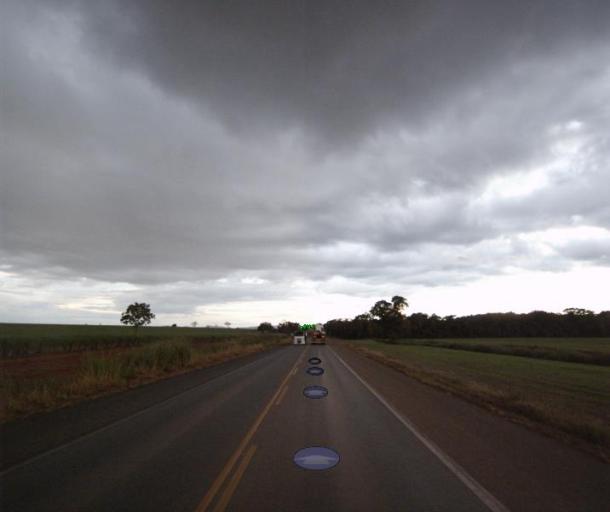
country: BR
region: Goias
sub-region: Uruacu
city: Uruacu
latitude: -14.6520
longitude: -49.1873
